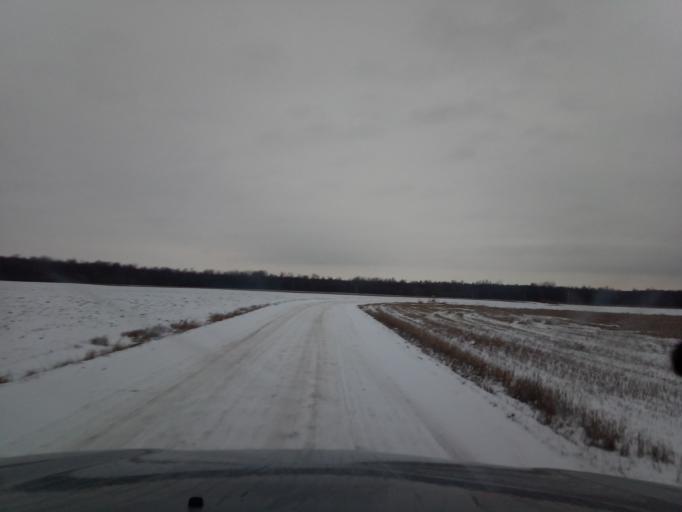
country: LT
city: Ramygala
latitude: 55.4836
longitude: 24.5675
